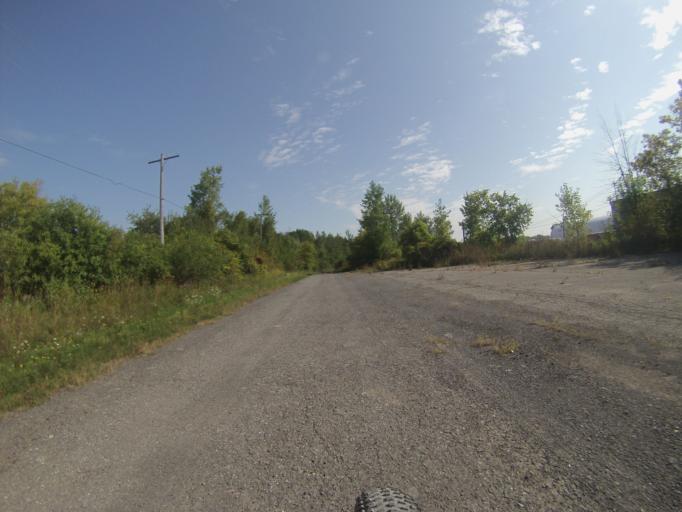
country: CA
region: Ontario
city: Ottawa
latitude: 45.3694
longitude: -75.6461
